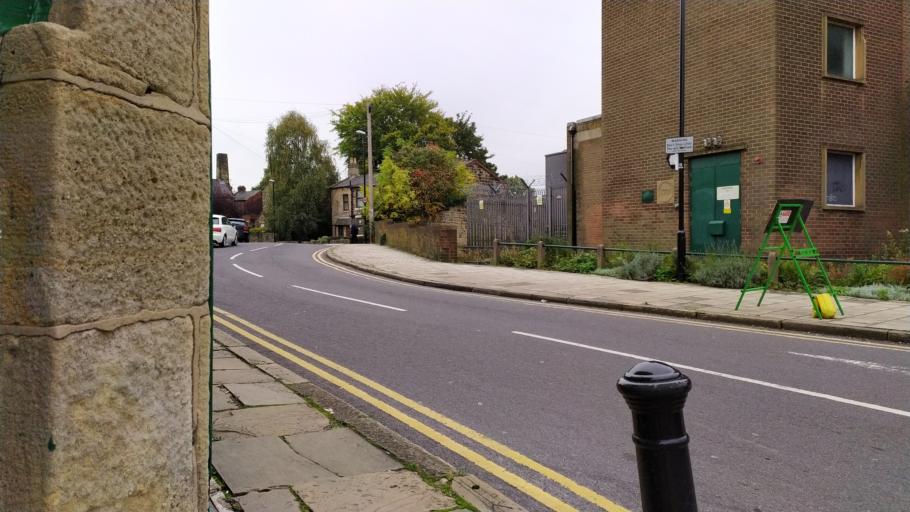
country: GB
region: England
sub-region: City and Borough of Leeds
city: Chapel Allerton
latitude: 53.8282
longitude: -1.5821
